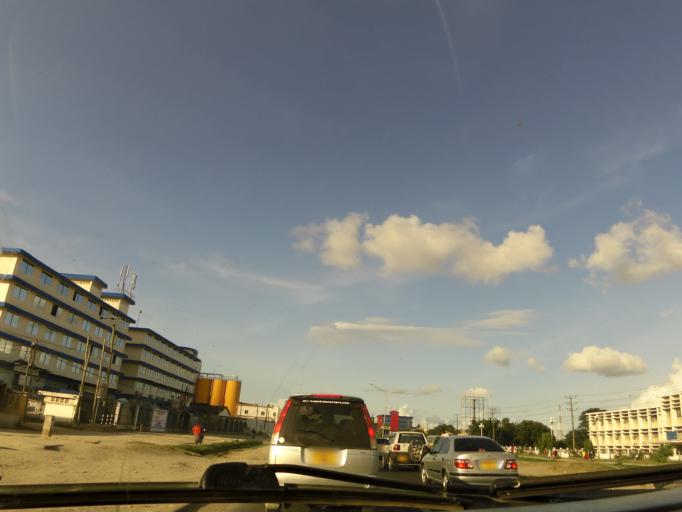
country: TZ
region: Dar es Salaam
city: Dar es Salaam
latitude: -6.8452
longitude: 39.2429
